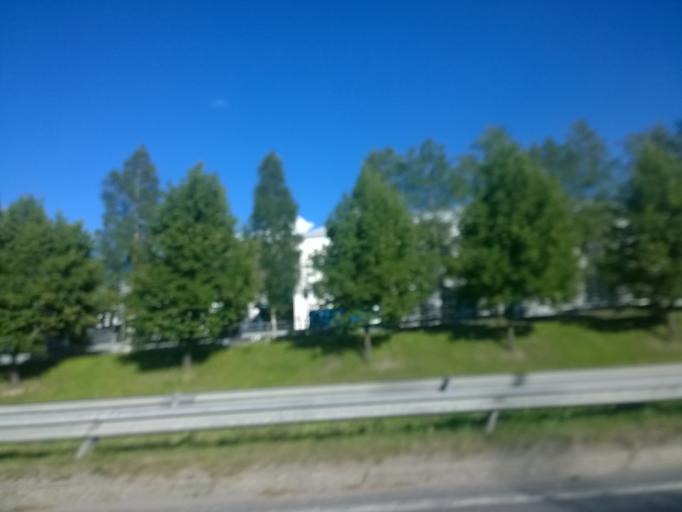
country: FI
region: Pirkanmaa
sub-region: Tampere
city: Tampere
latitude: 61.4798
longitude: 23.7751
